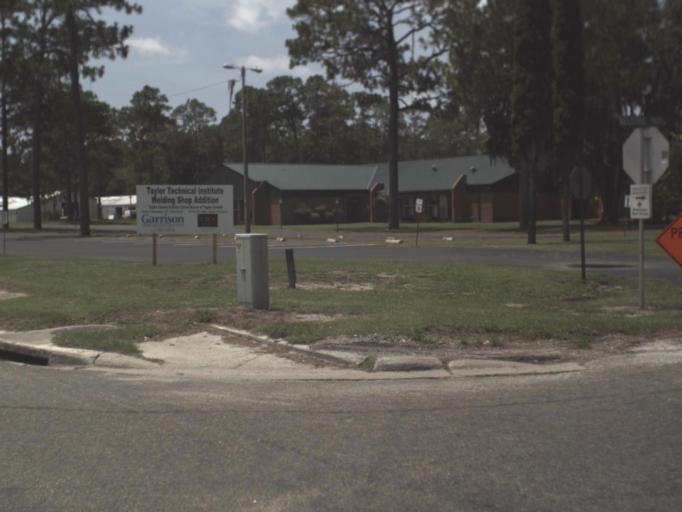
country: US
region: Florida
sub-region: Taylor County
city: Perry
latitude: 30.0791
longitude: -83.5655
